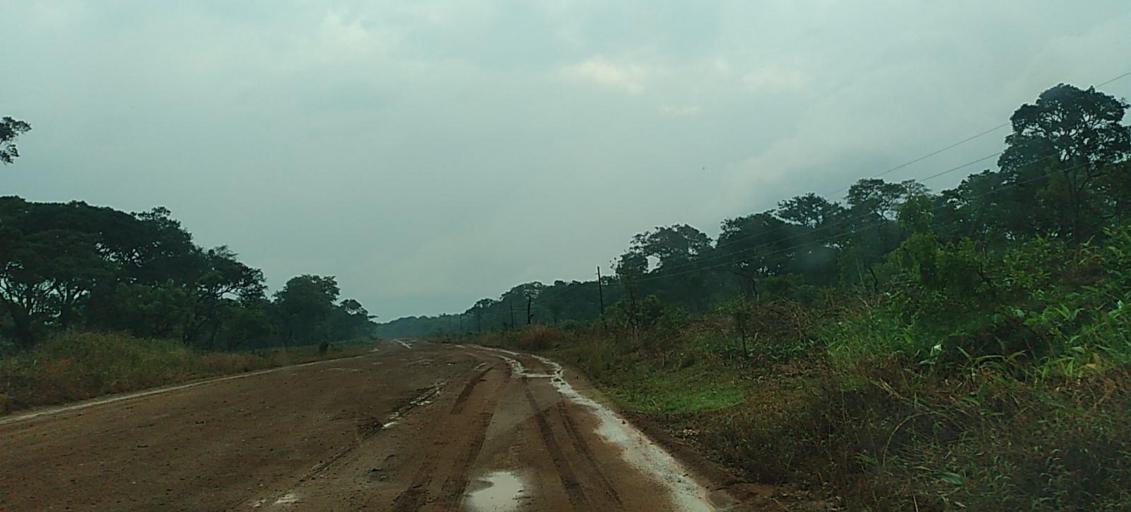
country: ZM
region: North-Western
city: Mwinilunga
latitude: -11.5817
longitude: 24.3897
